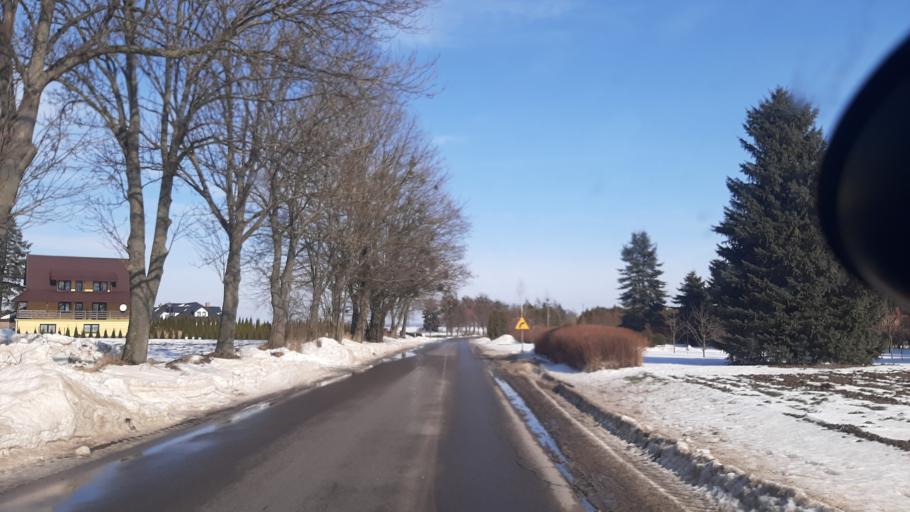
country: PL
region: Lublin Voivodeship
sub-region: Powiat pulawski
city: Kurow
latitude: 51.3777
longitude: 22.1561
